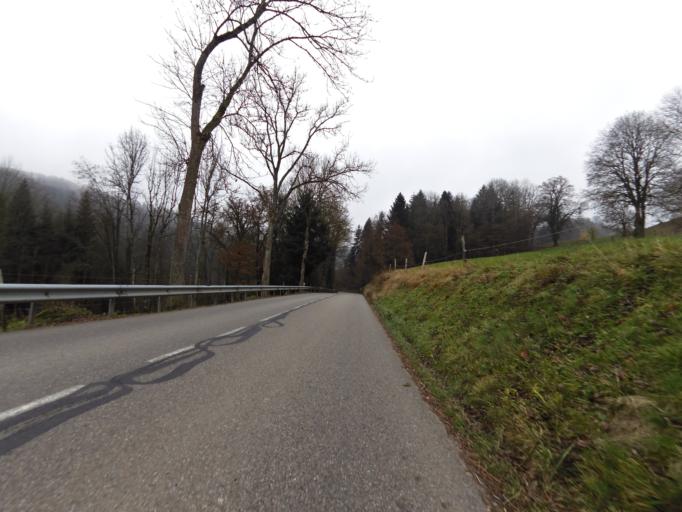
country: CH
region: Jura
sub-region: Delemont District
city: Bassecourt
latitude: 47.4236
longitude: 7.2457
